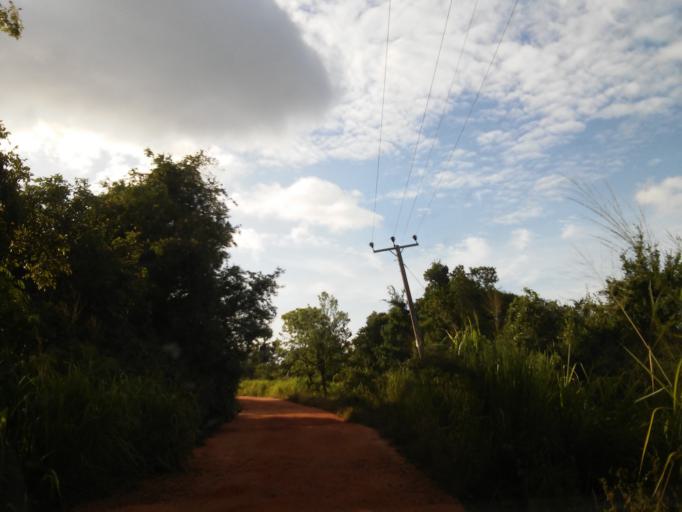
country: LK
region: Central
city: Sigiriya
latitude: 8.1700
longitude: 80.6831
